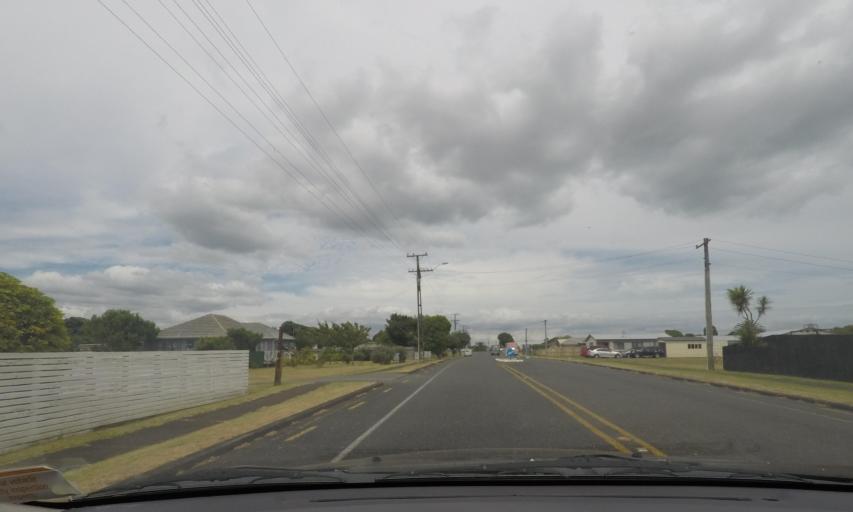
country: NZ
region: Auckland
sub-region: Auckland
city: Mangere
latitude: -36.9828
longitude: 174.7632
